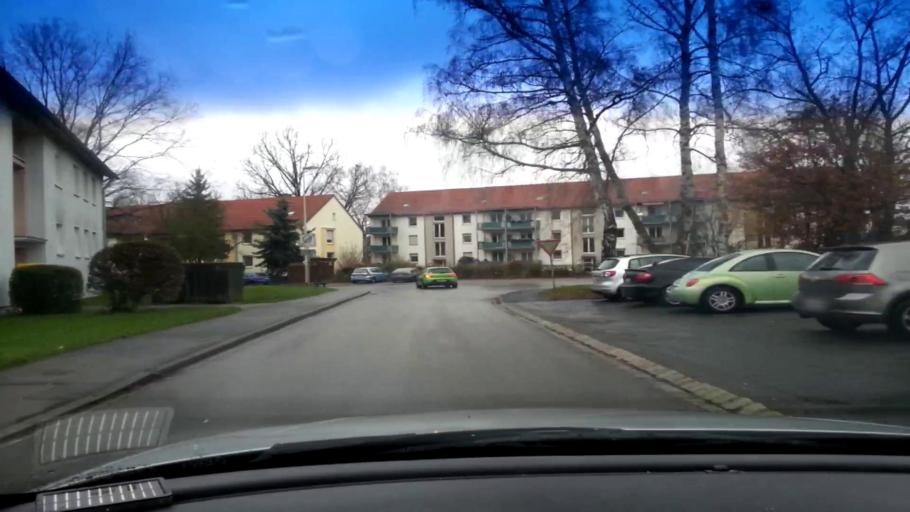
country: DE
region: Bavaria
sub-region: Upper Franconia
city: Gundelsheim
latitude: 49.9250
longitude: 10.9295
